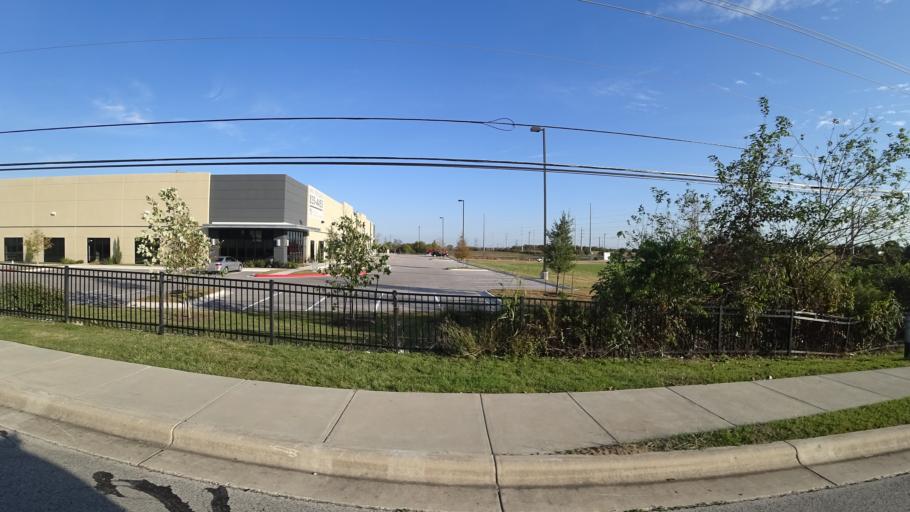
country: US
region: Texas
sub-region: Travis County
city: Pflugerville
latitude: 30.4106
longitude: -97.6478
